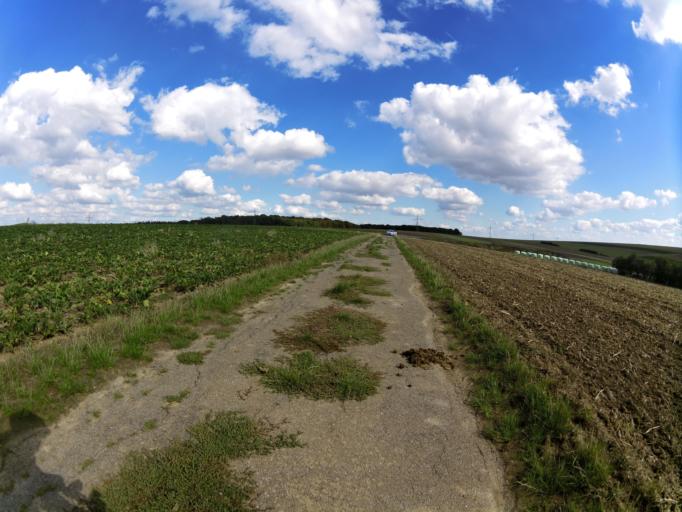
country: DE
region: Bavaria
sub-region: Regierungsbezirk Unterfranken
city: Frickenhausen
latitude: 49.6918
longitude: 10.0924
